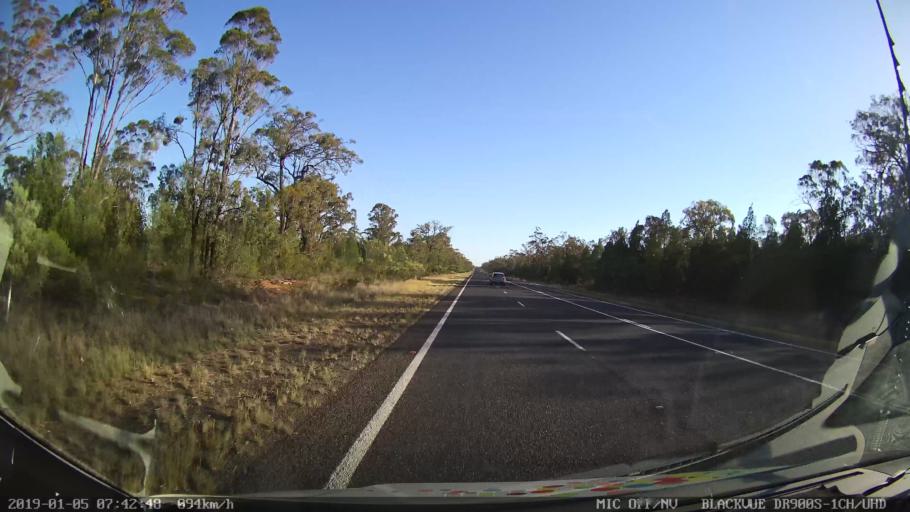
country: AU
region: New South Wales
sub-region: Gilgandra
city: Gilgandra
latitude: -31.8932
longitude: 148.6295
